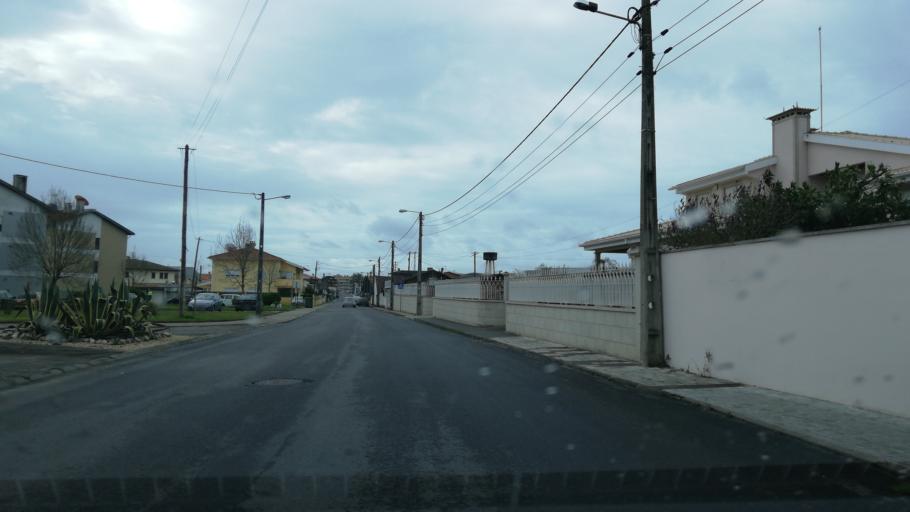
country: PT
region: Aveiro
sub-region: Agueda
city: Agueda
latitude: 40.5955
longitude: -8.4507
